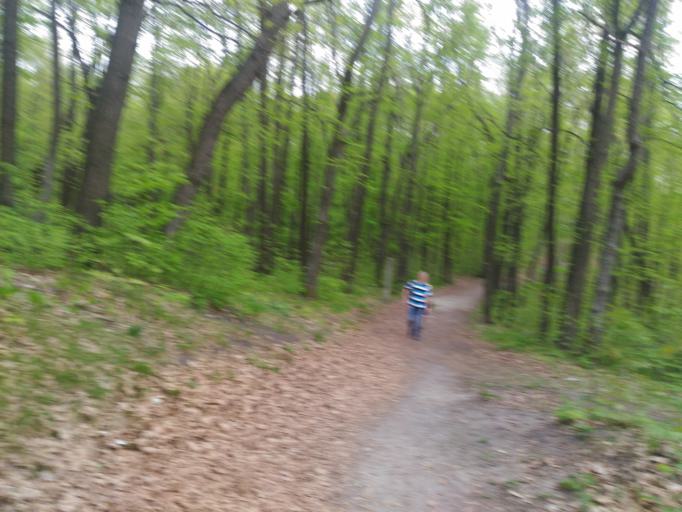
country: RU
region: Ulyanovsk
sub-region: Ulyanovskiy Rayon
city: Ulyanovsk
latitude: 54.2729
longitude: 48.3411
